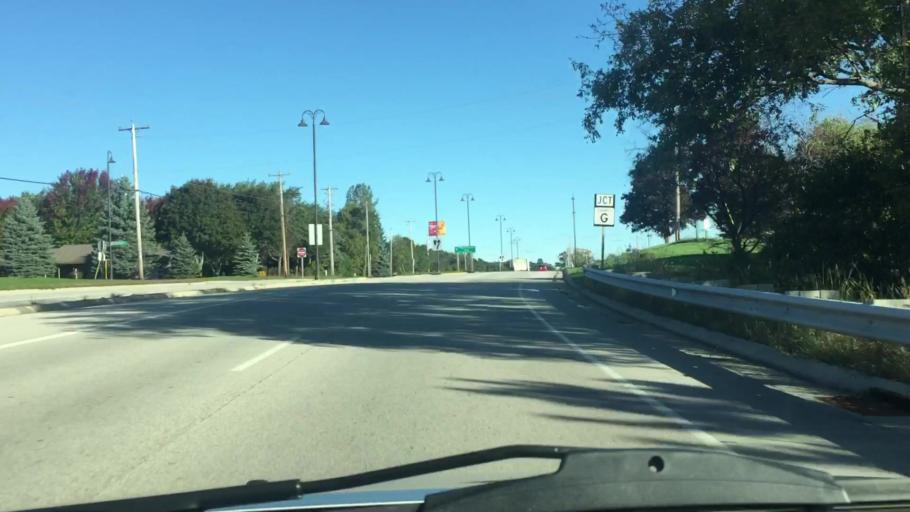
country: US
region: Wisconsin
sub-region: Waukesha County
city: Wales
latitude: 42.9927
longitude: -88.3842
